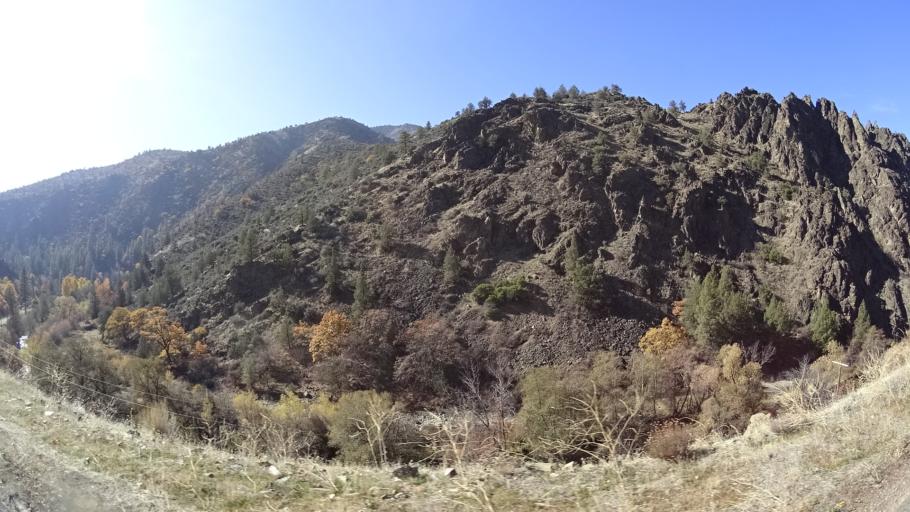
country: US
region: California
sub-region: Siskiyou County
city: Yreka
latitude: 41.8271
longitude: -122.5931
